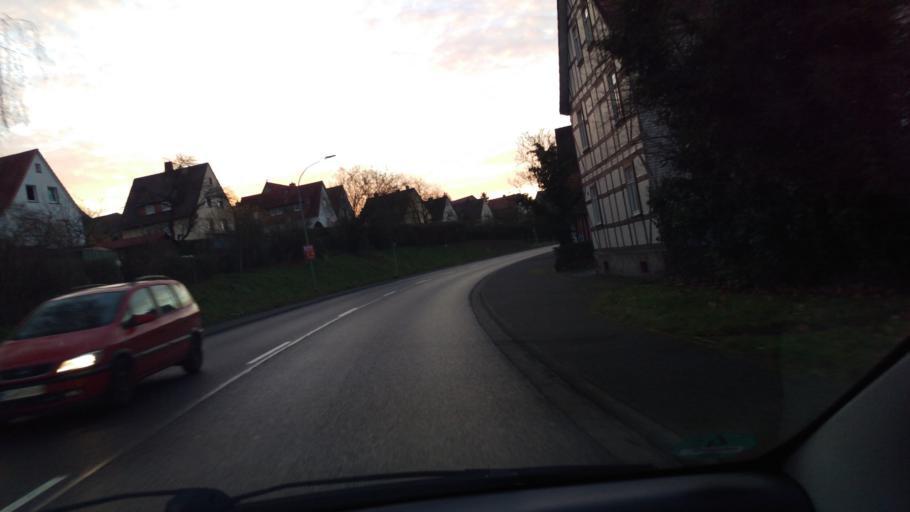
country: DE
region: Hesse
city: Kirtorf
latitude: 50.7568
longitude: 9.1332
